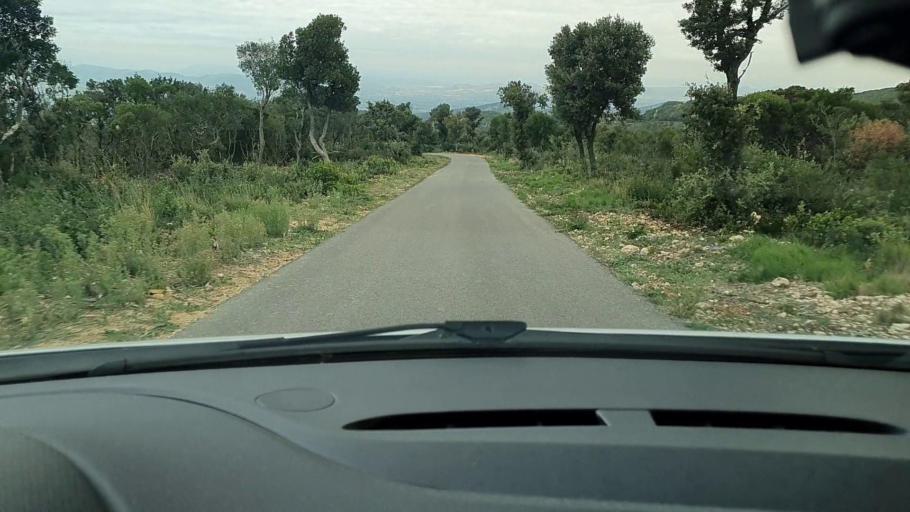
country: FR
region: Languedoc-Roussillon
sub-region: Departement du Gard
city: Mons
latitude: 44.1370
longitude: 4.2799
